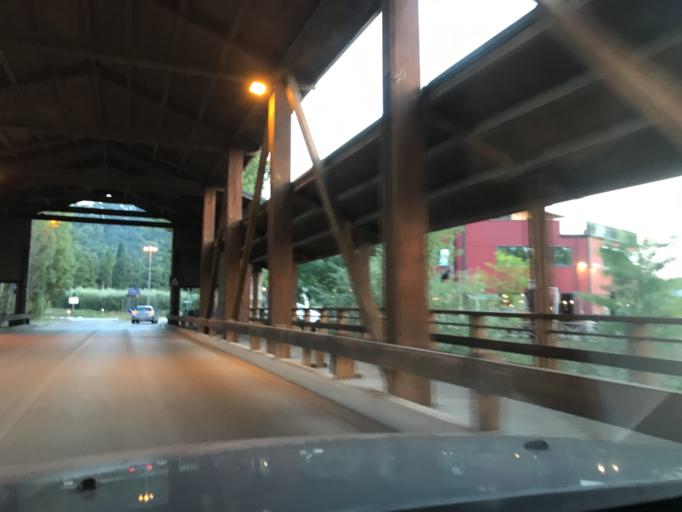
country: IT
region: Umbria
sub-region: Provincia di Perugia
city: Via Lippia
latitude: 43.0908
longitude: 12.4502
